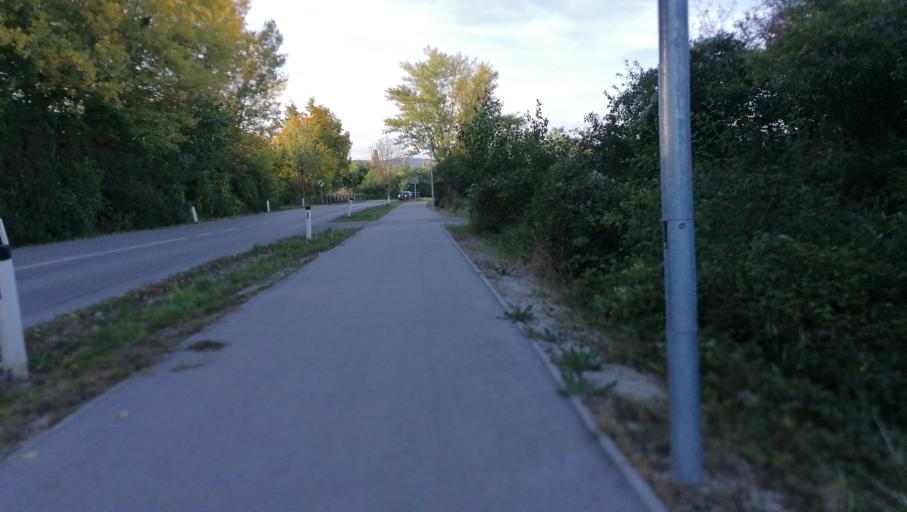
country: AT
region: Lower Austria
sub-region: Politischer Bezirk Baden
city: Pfaffstatten
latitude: 47.9862
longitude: 16.2607
